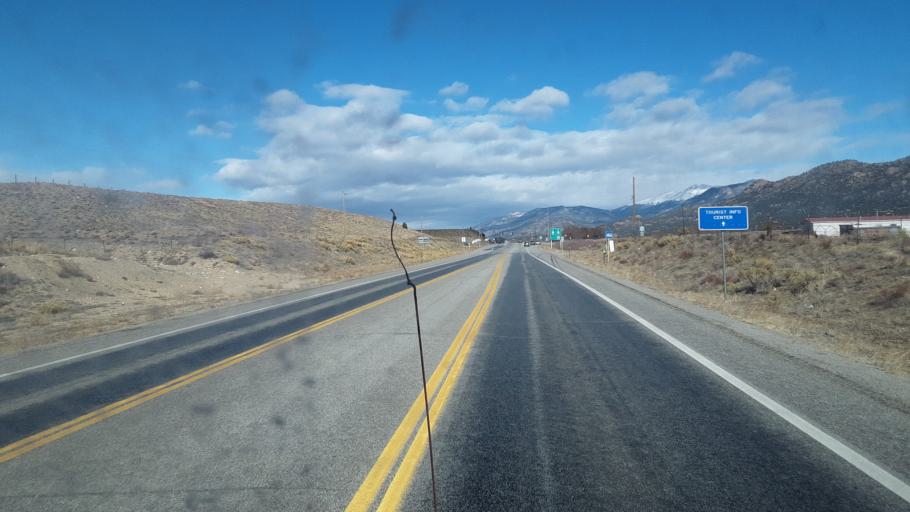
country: US
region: Colorado
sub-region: Chaffee County
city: Buena Vista
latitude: 38.8050
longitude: -106.1147
